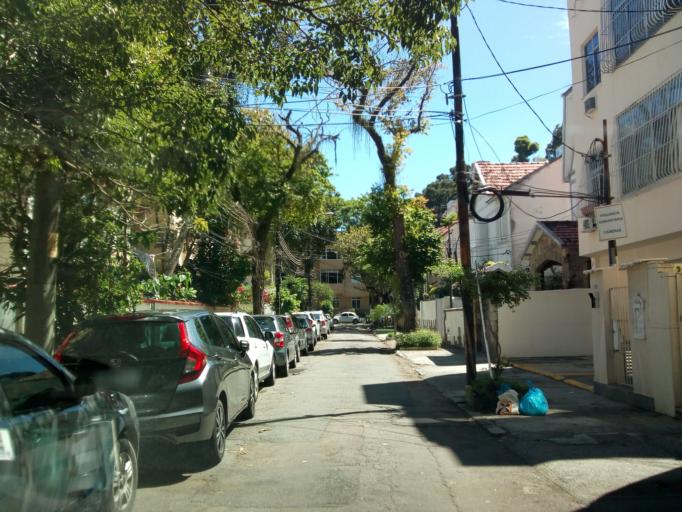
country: BR
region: Rio de Janeiro
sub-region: Rio De Janeiro
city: Rio de Janeiro
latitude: -22.9458
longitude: -43.1610
